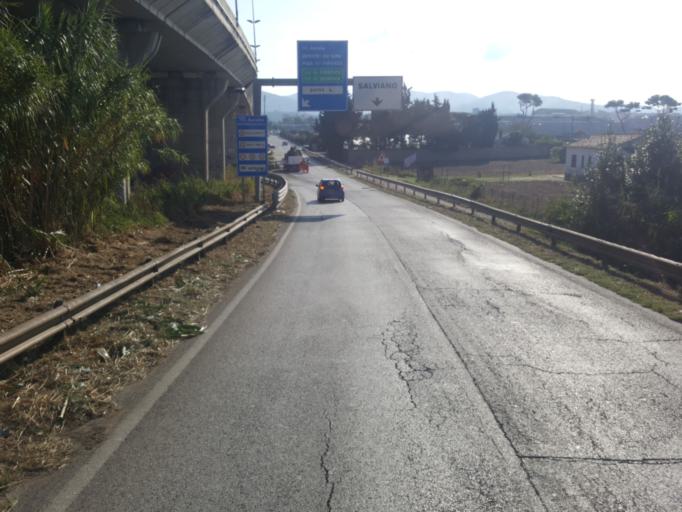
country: IT
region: Tuscany
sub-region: Provincia di Livorno
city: Livorno
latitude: 43.5315
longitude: 10.3342
